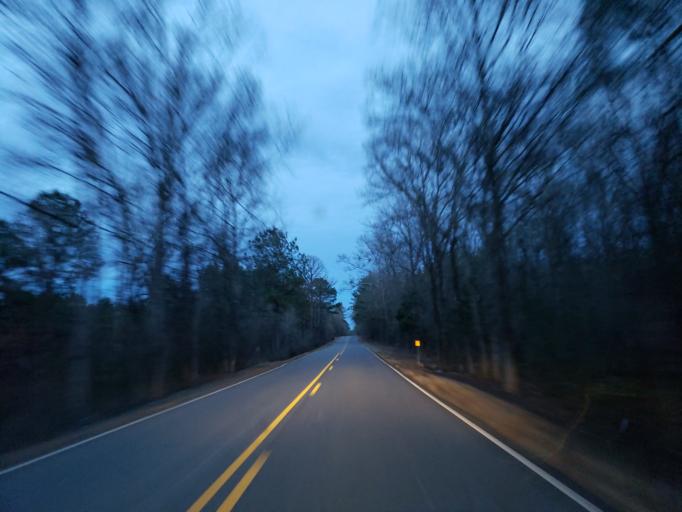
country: US
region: Alabama
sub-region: Greene County
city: Eutaw
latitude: 32.8853
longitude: -88.0550
